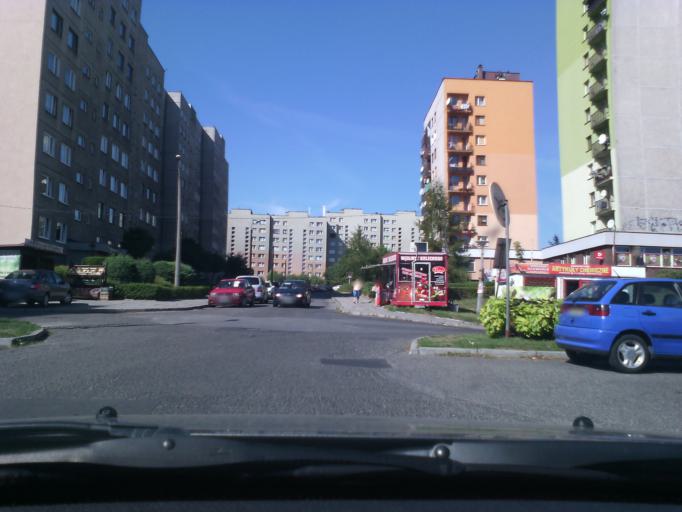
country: PL
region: Silesian Voivodeship
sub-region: Rybnik
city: Rybnik
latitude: 50.0868
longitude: 18.5298
